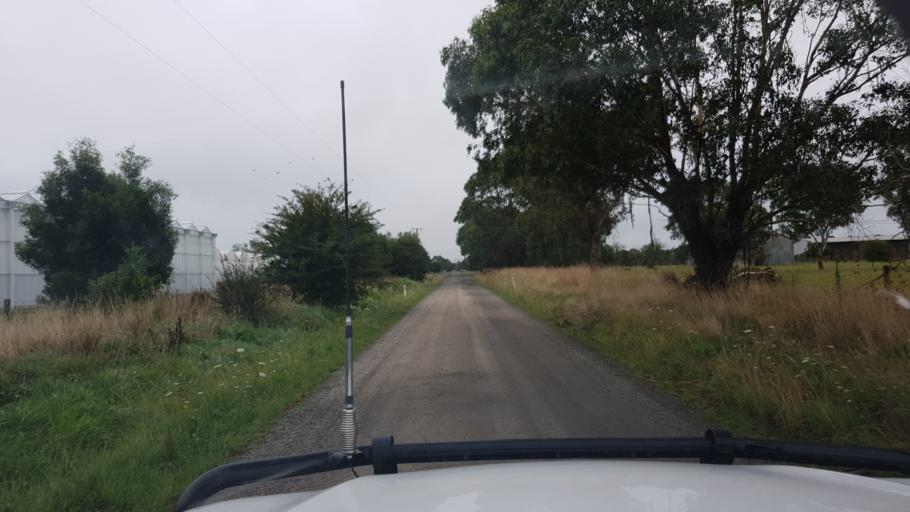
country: AU
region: Victoria
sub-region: Latrobe
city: Moe
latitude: -38.1894
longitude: 146.0963
